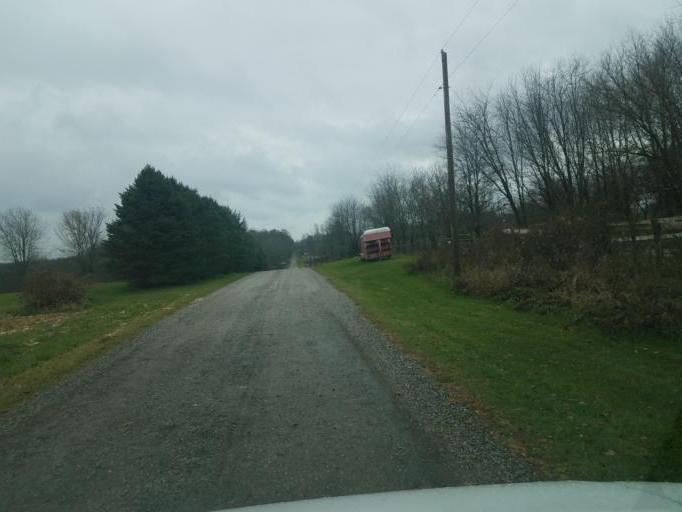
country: US
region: Ohio
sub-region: Morrow County
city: Mount Gilead
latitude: 40.5290
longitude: -82.7015
